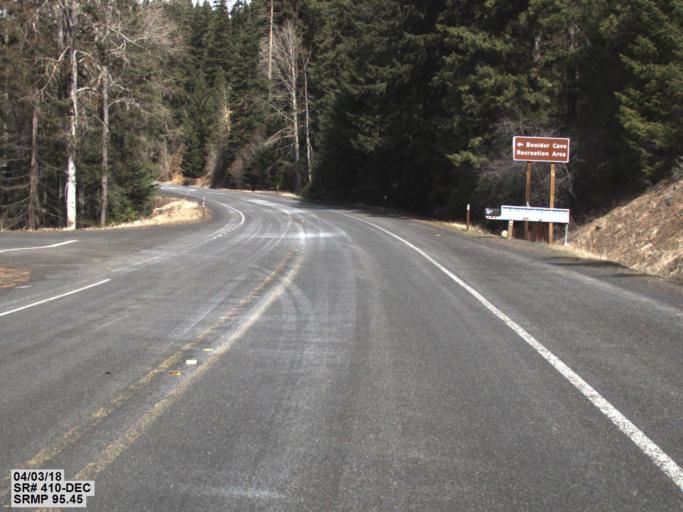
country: US
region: Washington
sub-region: Kittitas County
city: Cle Elum
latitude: 46.9501
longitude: -121.0707
